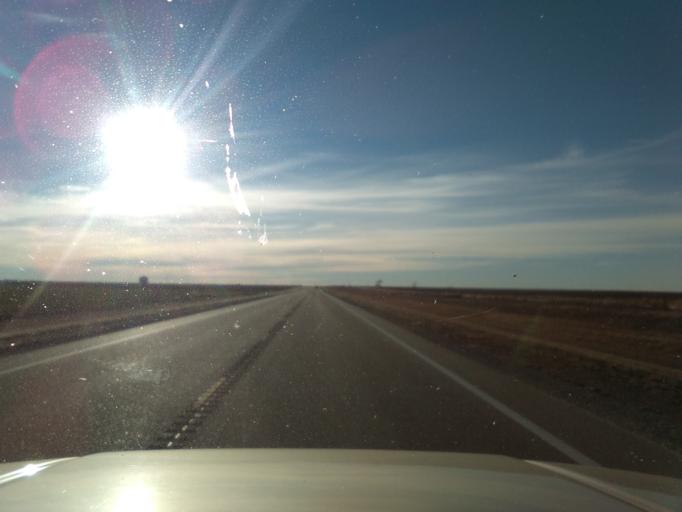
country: US
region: Kansas
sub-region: Sheridan County
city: Hoxie
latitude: 39.4997
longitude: -100.6702
